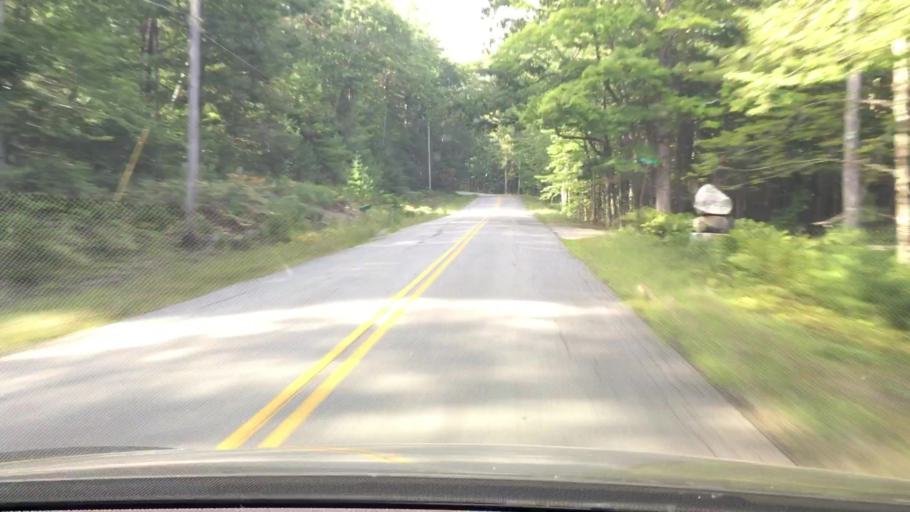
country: US
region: Maine
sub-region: Hancock County
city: Orland
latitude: 44.5288
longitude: -68.7636
